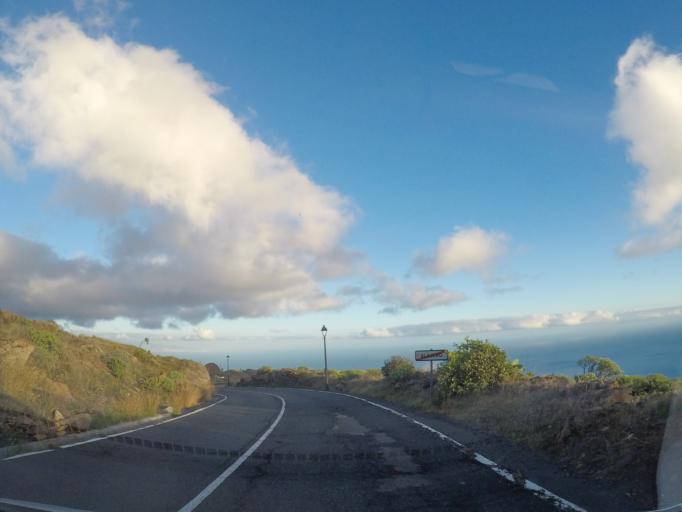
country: ES
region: Canary Islands
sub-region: Provincia de Santa Cruz de Tenerife
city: Alajero
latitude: 28.0569
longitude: -17.2329
